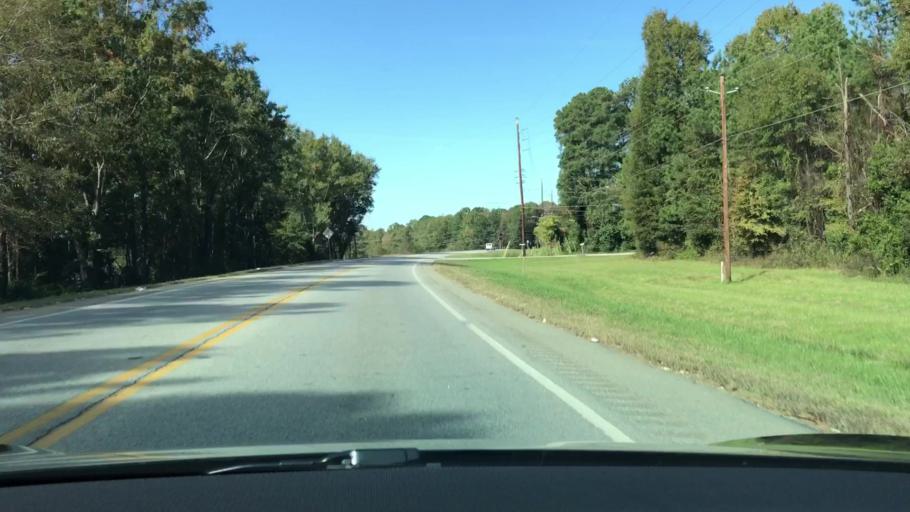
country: US
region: Georgia
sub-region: Warren County
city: Warrenton
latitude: 33.4002
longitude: -82.6649
